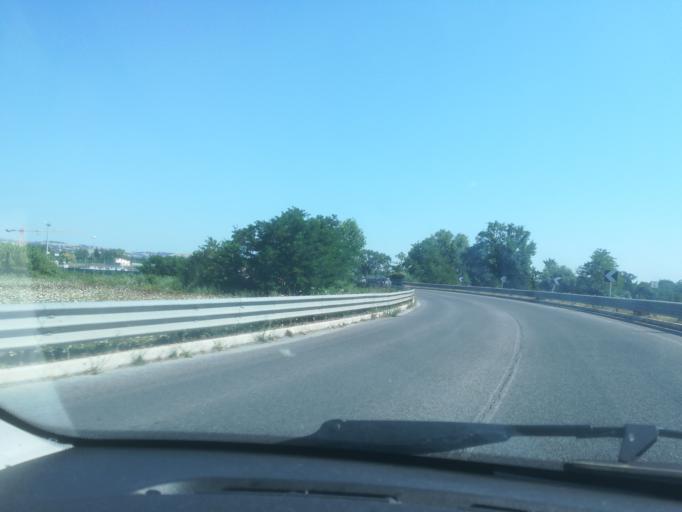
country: IT
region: The Marches
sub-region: Provincia di Macerata
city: Villa Potenza
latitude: 43.3216
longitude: 13.4293
